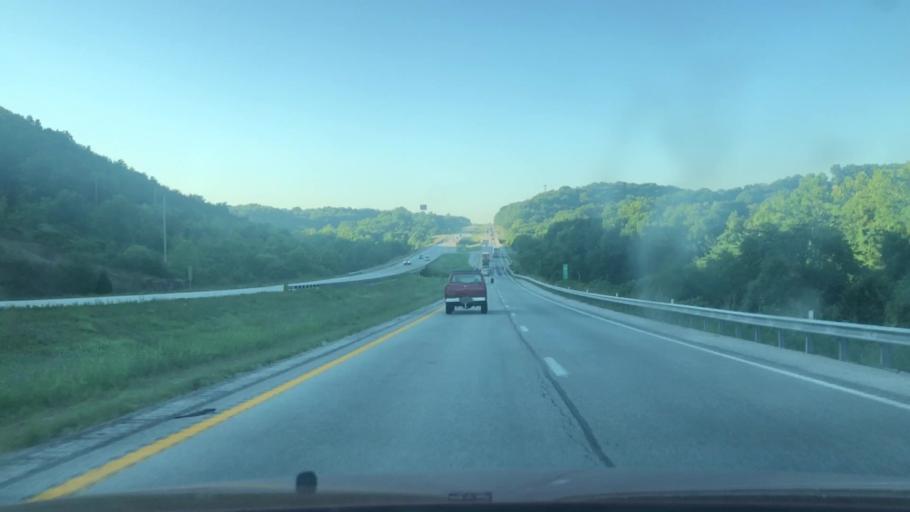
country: US
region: Missouri
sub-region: Christian County
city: Ozark
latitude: 36.9107
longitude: -93.2445
